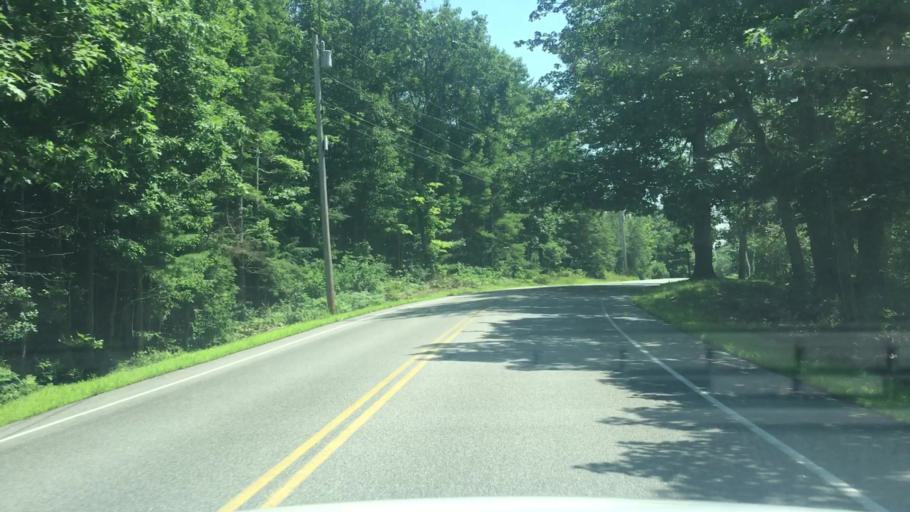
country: US
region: Maine
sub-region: Cumberland County
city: Falmouth
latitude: 43.7463
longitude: -70.2582
